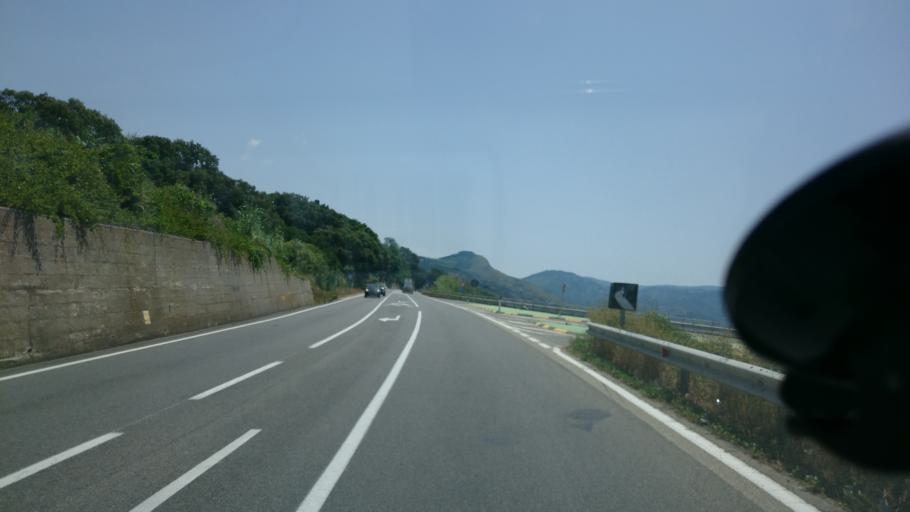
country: IT
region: Calabria
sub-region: Provincia di Cosenza
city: Cittadella del Capo
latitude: 39.5394
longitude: 15.8967
